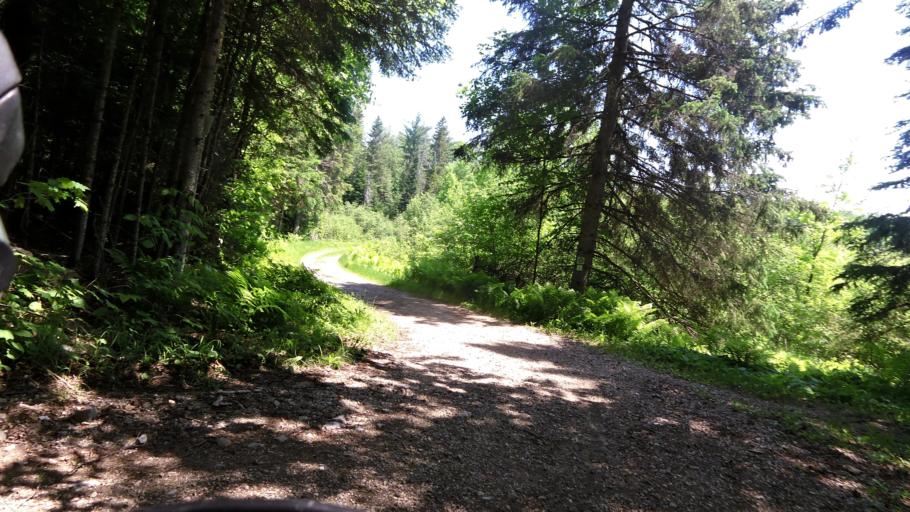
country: CA
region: Quebec
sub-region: Outaouais
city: Wakefield
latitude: 45.5669
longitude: -75.9283
